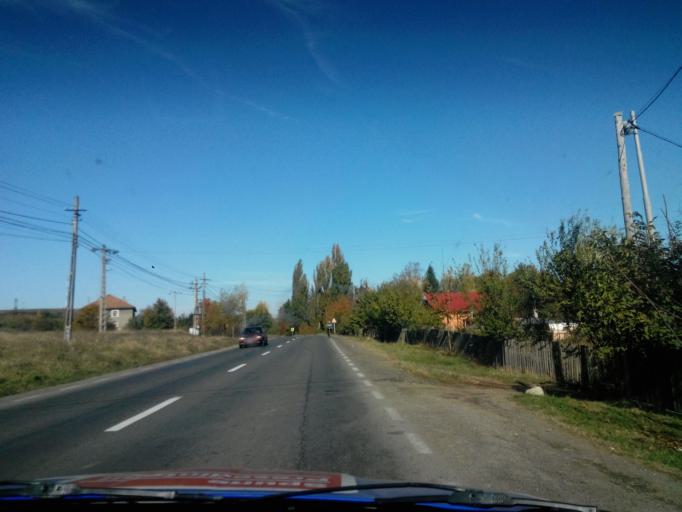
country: RO
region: Bacau
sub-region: Comuna Stefan Cel Mare
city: Stefan Cel Mare
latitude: 46.2191
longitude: 26.8571
